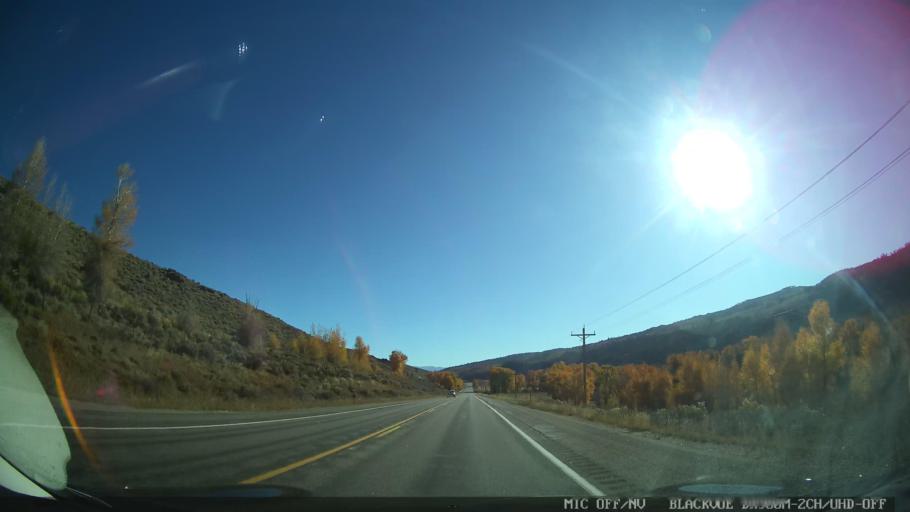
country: US
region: Colorado
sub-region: Grand County
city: Hot Sulphur Springs
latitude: 40.0984
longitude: -106.0439
